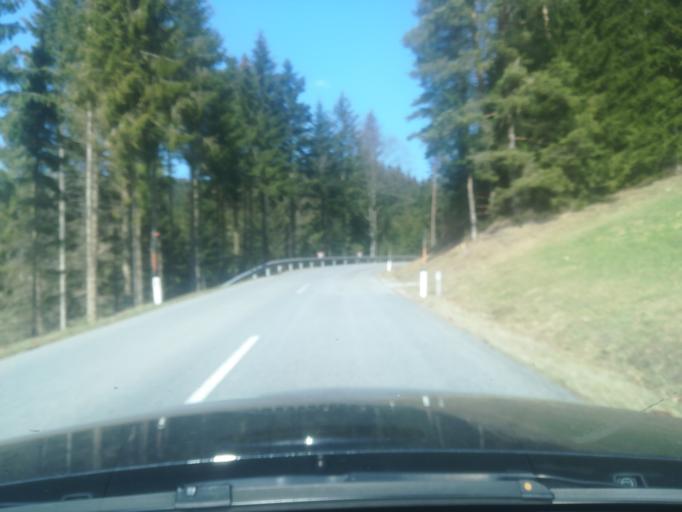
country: AT
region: Lower Austria
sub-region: Politischer Bezirk Zwettl
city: Langschlag
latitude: 48.4711
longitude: 14.7981
